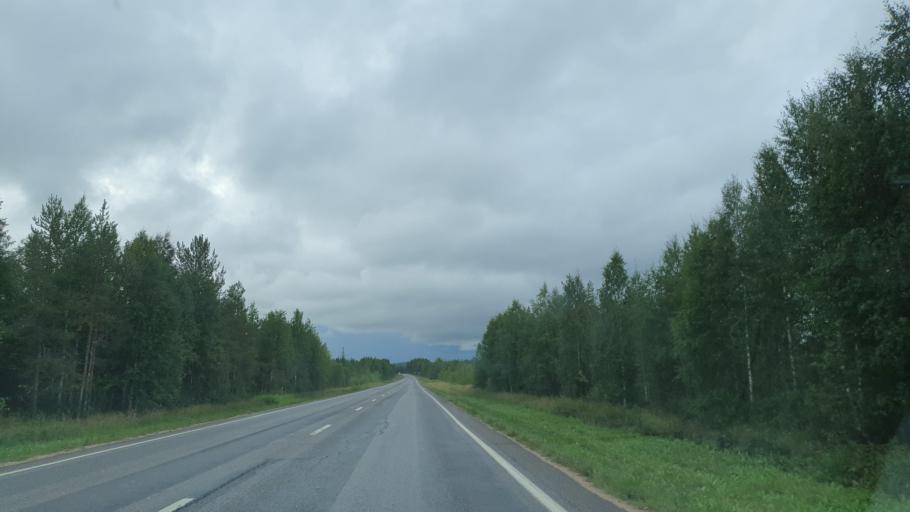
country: FI
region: Lapland
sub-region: Tunturi-Lappi
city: Kolari
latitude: 67.2184
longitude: 23.9026
